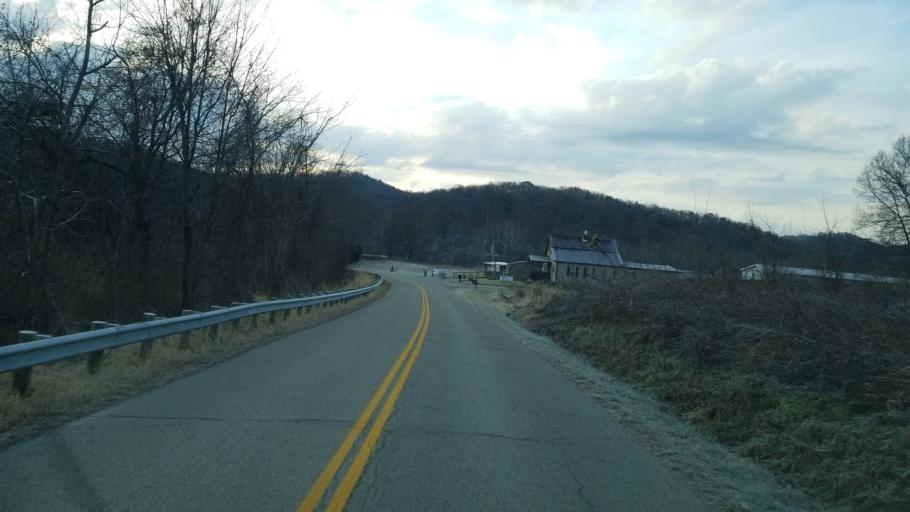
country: US
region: Ohio
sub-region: Ross County
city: Chillicothe
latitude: 39.2368
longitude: -82.8977
